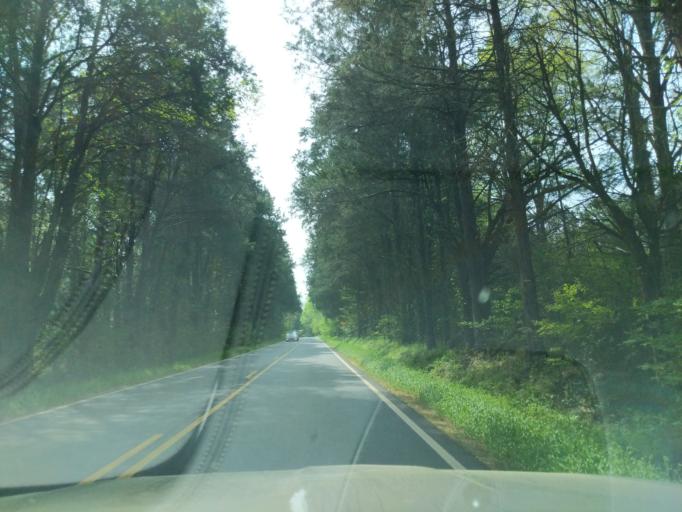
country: US
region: Georgia
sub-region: Columbia County
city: Appling
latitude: 33.6278
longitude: -82.3395
